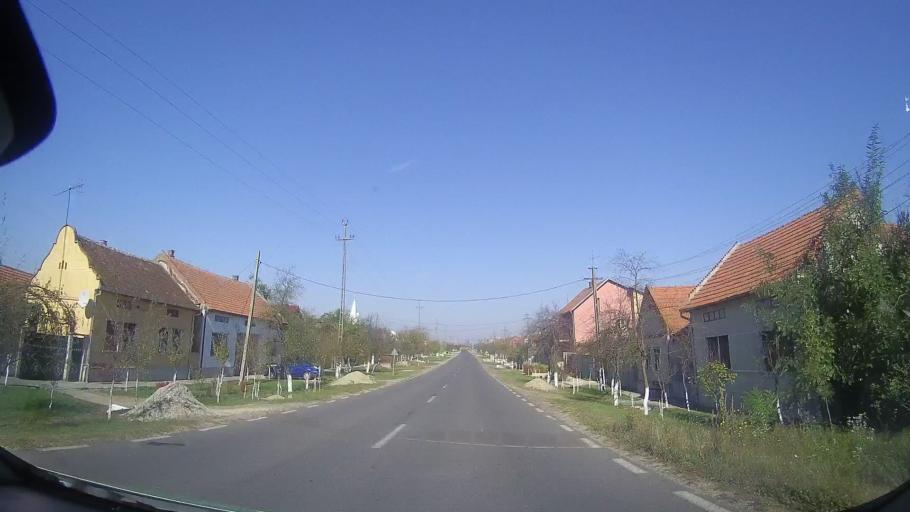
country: RO
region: Timis
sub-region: Comuna Costeiu
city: Costeiu
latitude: 45.7751
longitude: 21.8494
